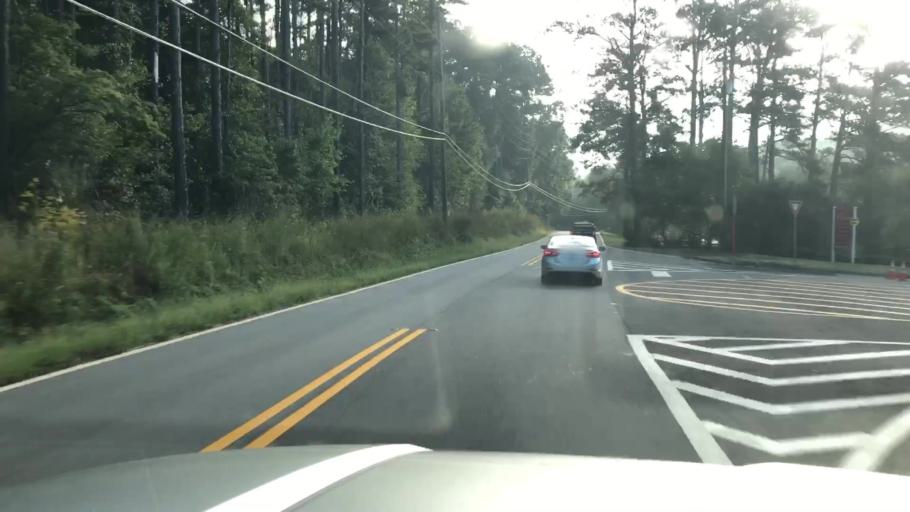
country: US
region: Georgia
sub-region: Bartow County
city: Emerson
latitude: 34.0798
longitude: -84.7503
